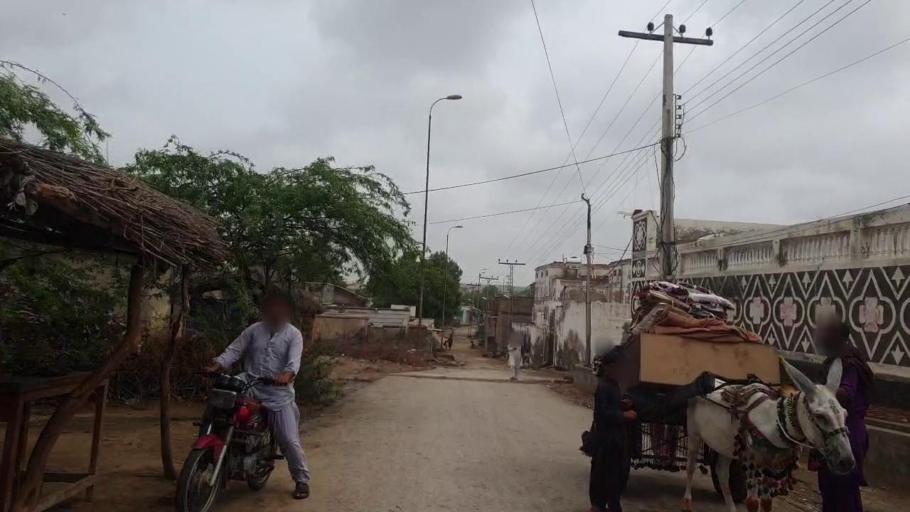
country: PK
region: Sindh
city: Diplo
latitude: 24.4635
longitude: 69.5818
